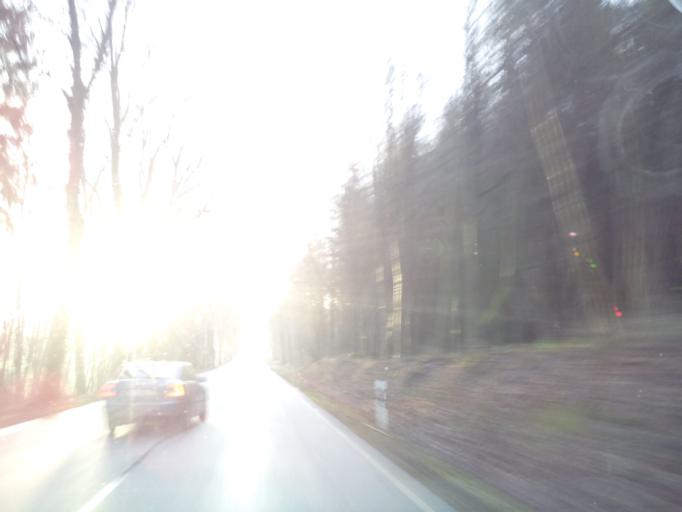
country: DE
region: Bavaria
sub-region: Upper Franconia
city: Lichtenfels
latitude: 50.1635
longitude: 11.0541
